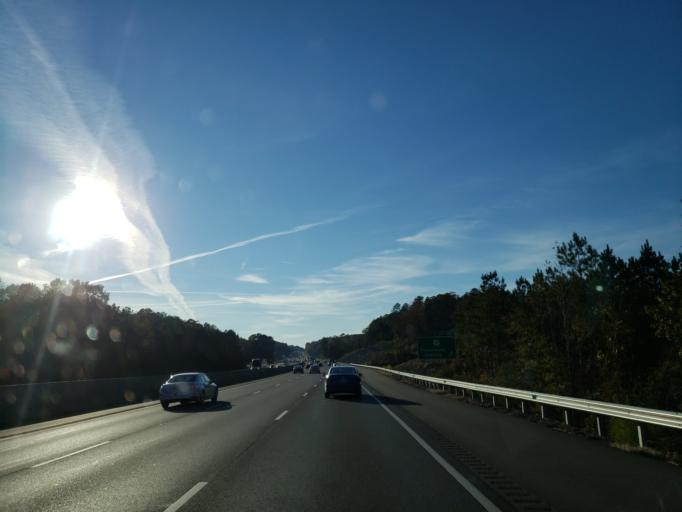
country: US
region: Alabama
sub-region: Tuscaloosa County
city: Coaling
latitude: 33.1758
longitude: -87.3986
